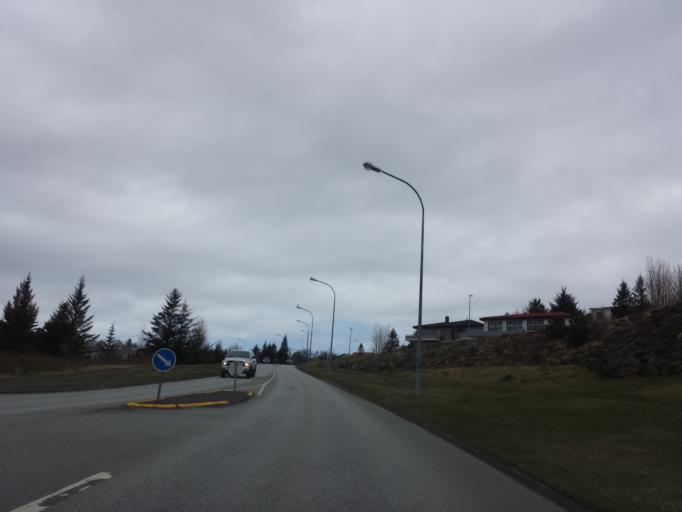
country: IS
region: Capital Region
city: Reykjavik
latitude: 64.1085
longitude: -21.8835
